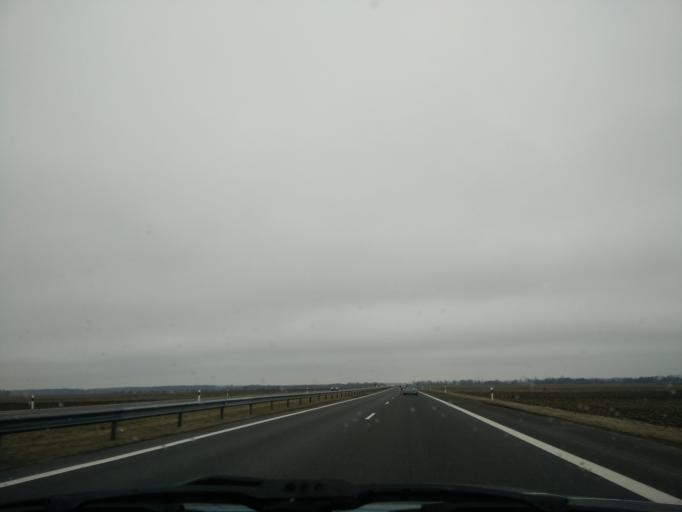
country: LT
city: Raseiniai
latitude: 55.3601
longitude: 23.0179
